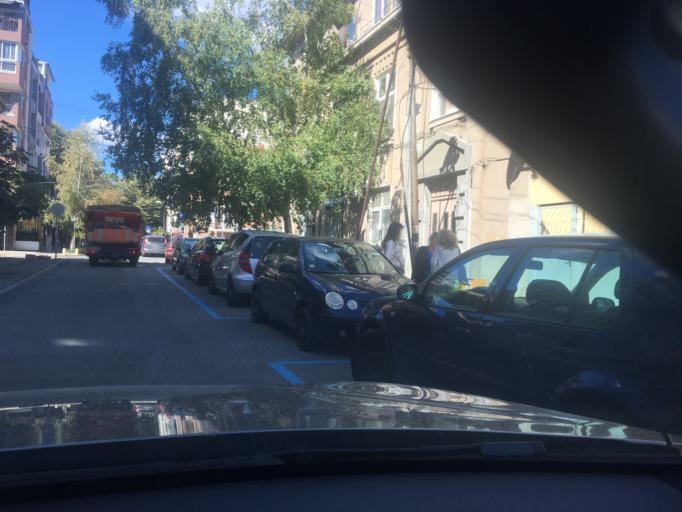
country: BG
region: Burgas
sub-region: Obshtina Burgas
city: Burgas
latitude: 42.4987
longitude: 27.4762
